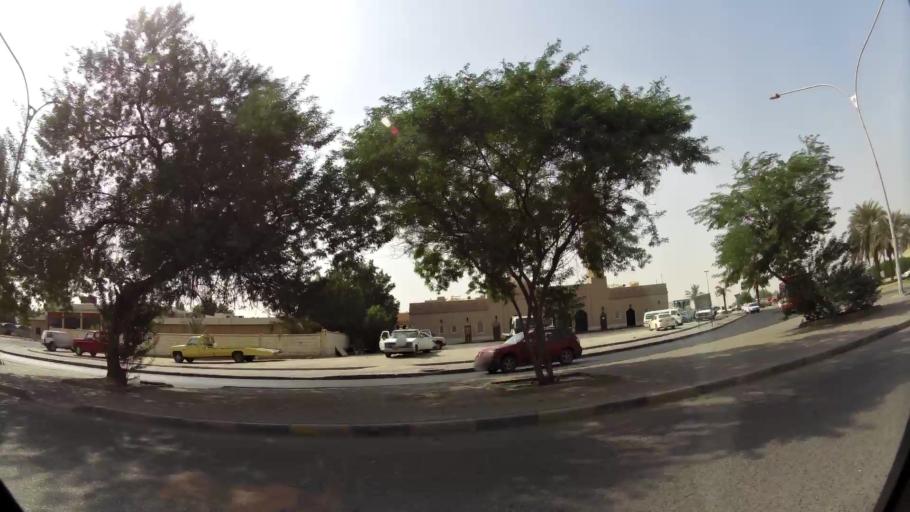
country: KW
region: Al Farwaniyah
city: Al Farwaniyah
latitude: 29.2544
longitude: 47.9244
